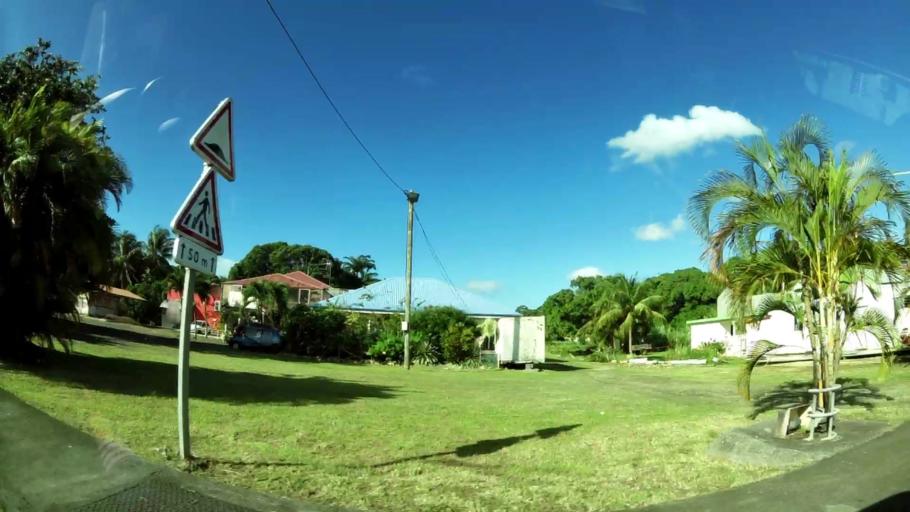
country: GP
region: Guadeloupe
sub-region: Guadeloupe
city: Le Moule
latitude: 16.3178
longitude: -61.4296
